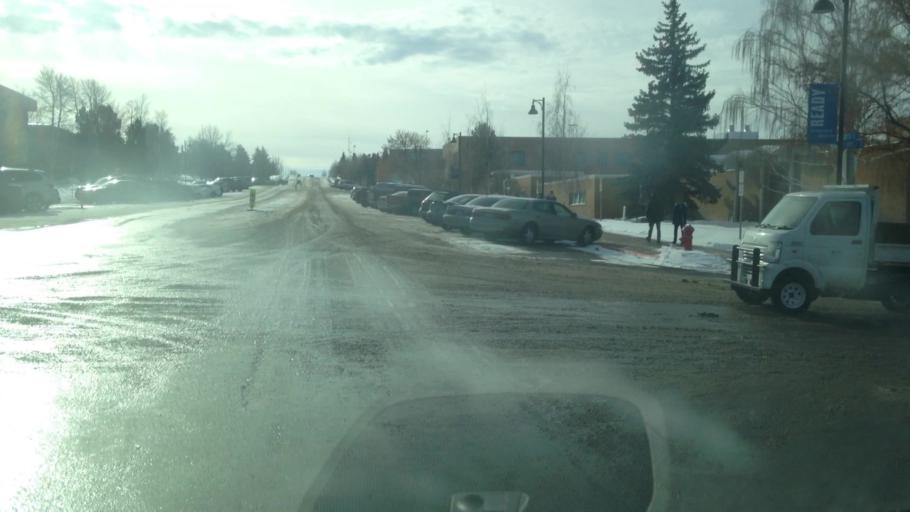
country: US
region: Idaho
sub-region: Madison County
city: Rexburg
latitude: 43.8166
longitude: -111.7839
